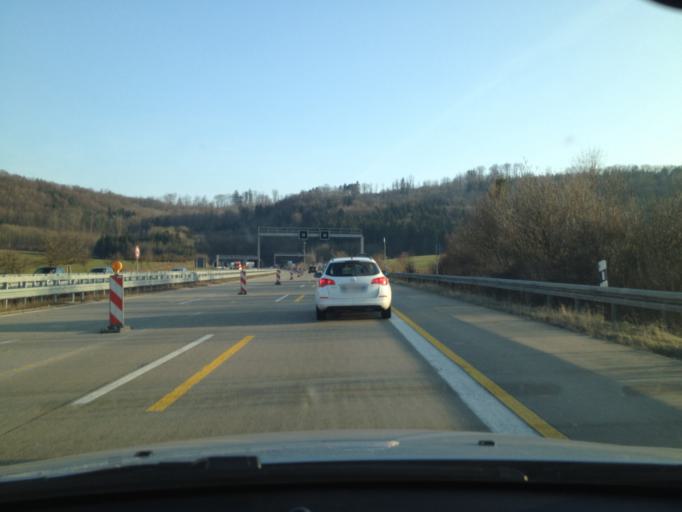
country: DE
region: Baden-Wuerttemberg
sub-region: Regierungsbezirk Stuttgart
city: Westhausen
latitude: 48.8792
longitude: 10.1650
